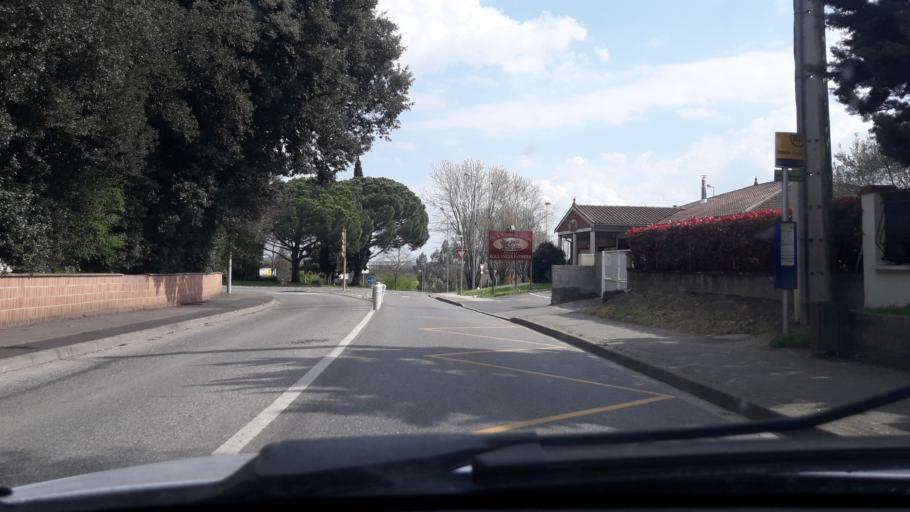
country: FR
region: Midi-Pyrenees
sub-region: Departement de la Haute-Garonne
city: Seysses
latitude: 43.4939
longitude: 1.3119
